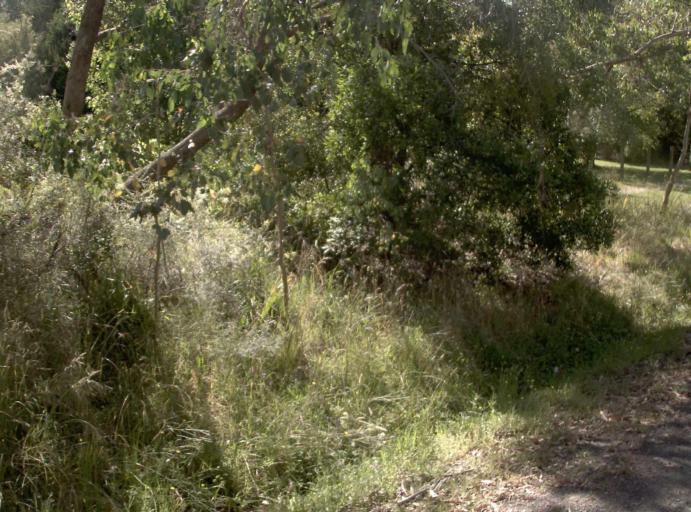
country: AU
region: Victoria
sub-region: Yarra Ranges
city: Healesville
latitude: -37.6654
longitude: 145.5337
